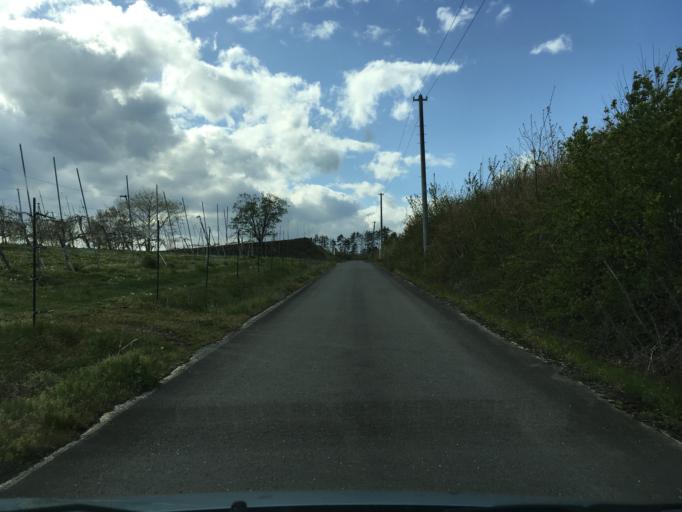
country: JP
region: Iwate
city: Ichinoseki
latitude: 38.7947
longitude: 141.4157
